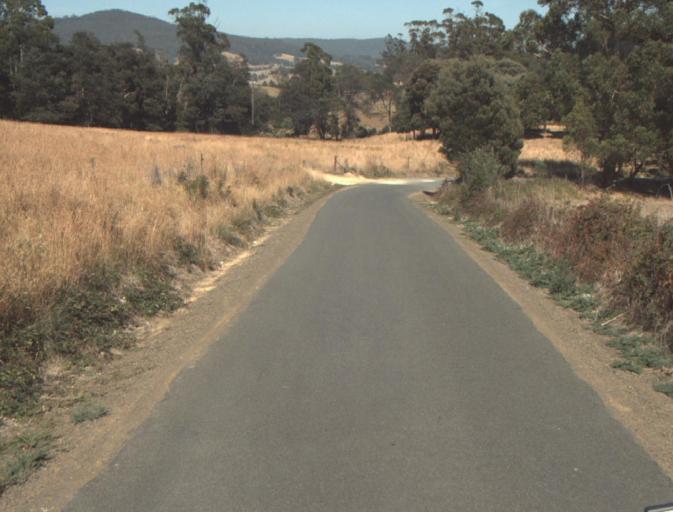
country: AU
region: Tasmania
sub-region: Launceston
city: Mayfield
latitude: -41.2313
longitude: 147.2439
